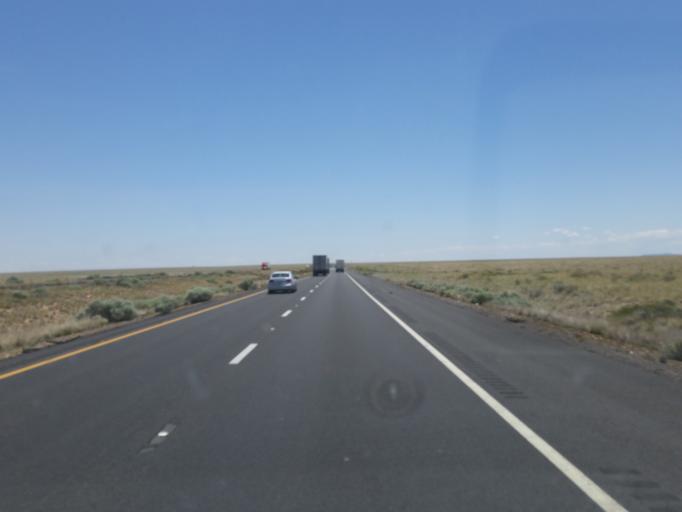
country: US
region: Arizona
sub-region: Coconino County
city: Flagstaff
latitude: 35.1467
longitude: -111.2324
